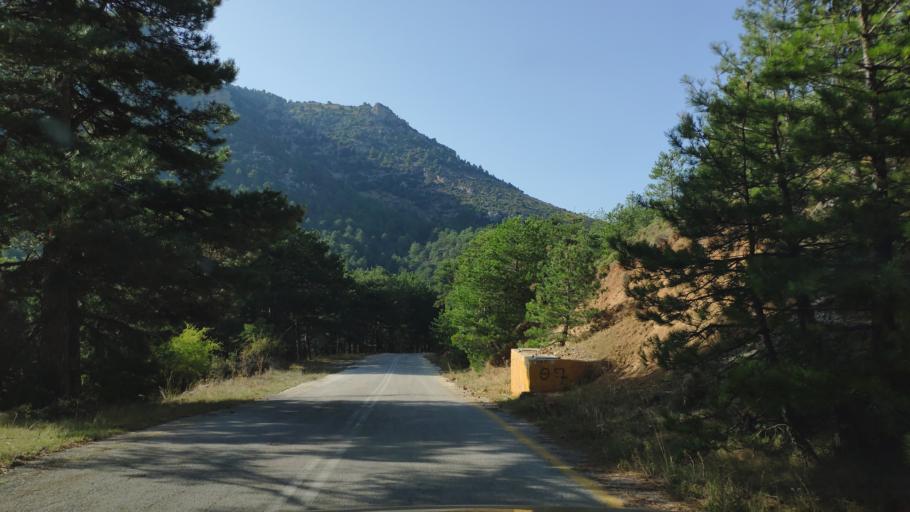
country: GR
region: West Greece
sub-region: Nomos Achaias
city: Aiyira
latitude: 38.0525
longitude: 22.3832
